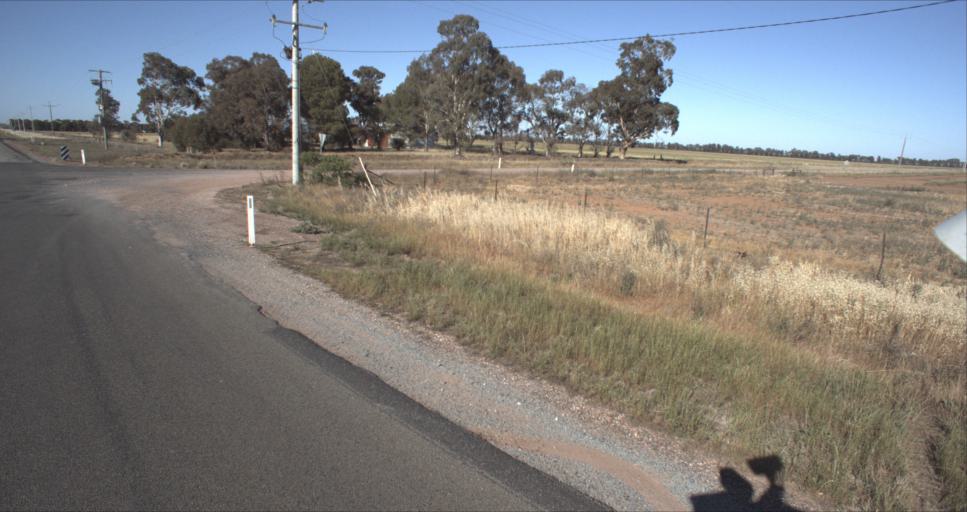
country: AU
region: New South Wales
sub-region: Leeton
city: Leeton
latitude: -34.5772
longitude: 146.2623
